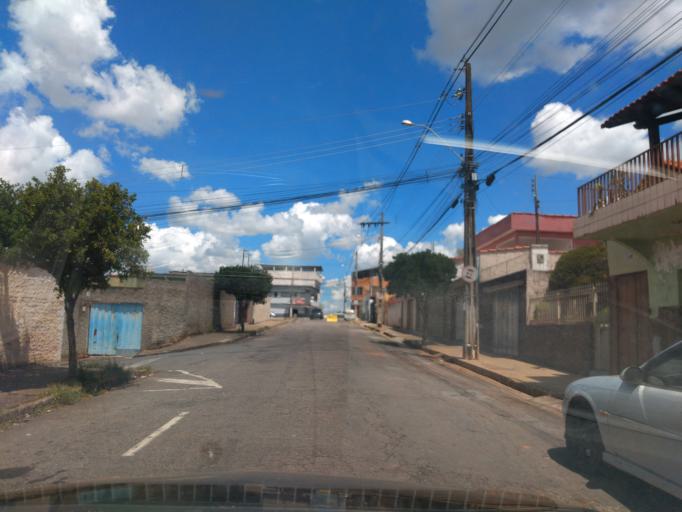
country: BR
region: Minas Gerais
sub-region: Tres Coracoes
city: Tres Coracoes
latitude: -21.6881
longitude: -45.2521
